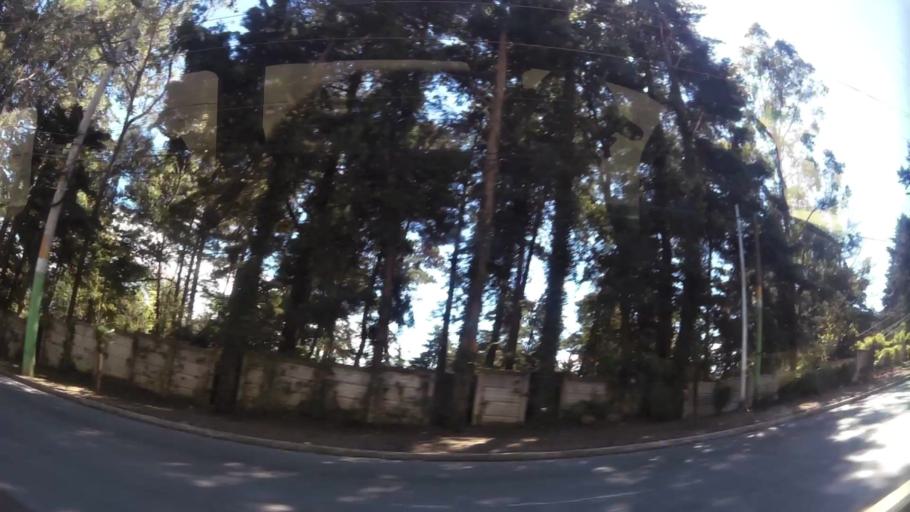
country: GT
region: Guatemala
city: San Jose Pinula
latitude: 14.5463
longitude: -90.4199
